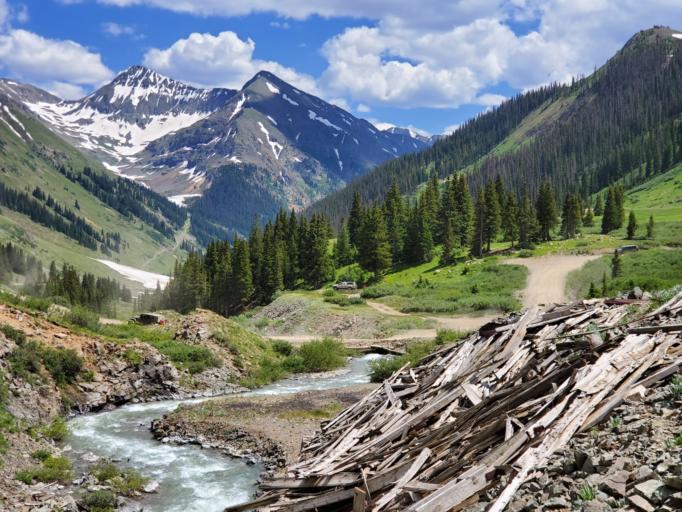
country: US
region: Colorado
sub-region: Ouray County
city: Ouray
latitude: 37.9309
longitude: -107.5686
